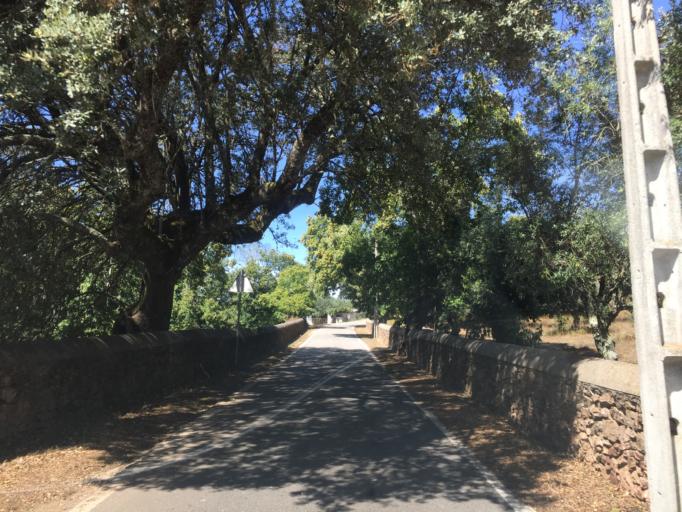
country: PT
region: Portalegre
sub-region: Marvao
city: Marvao
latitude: 39.3711
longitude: -7.3808
